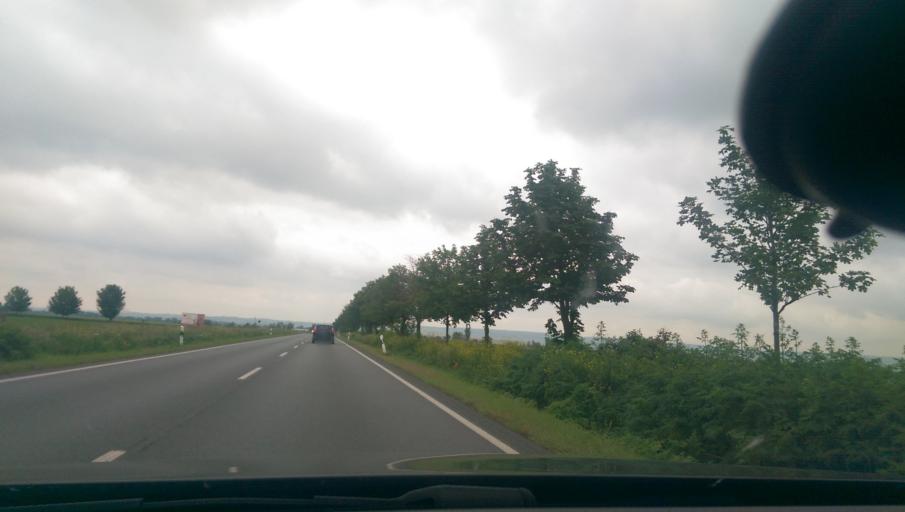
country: DE
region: Thuringia
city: Gebesee
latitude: 51.0996
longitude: 10.9293
